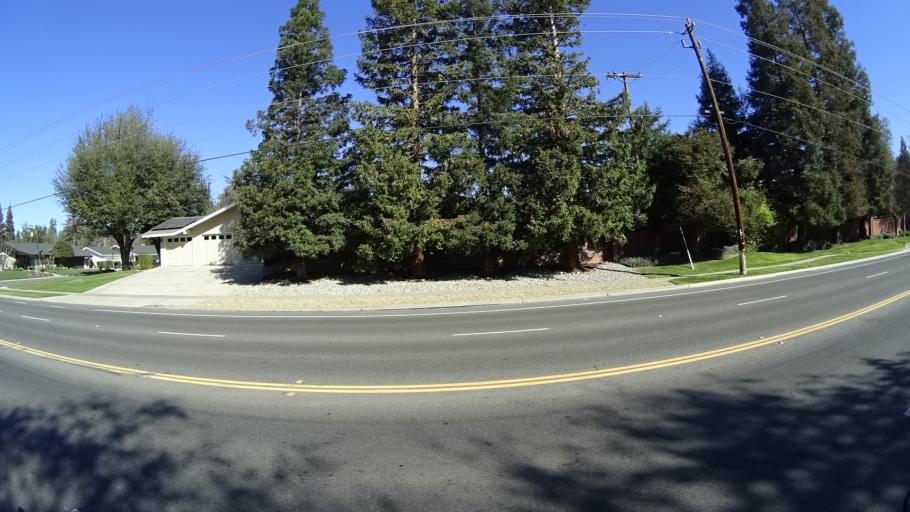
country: US
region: California
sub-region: Fresno County
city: Fresno
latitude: 36.8227
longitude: -119.8379
